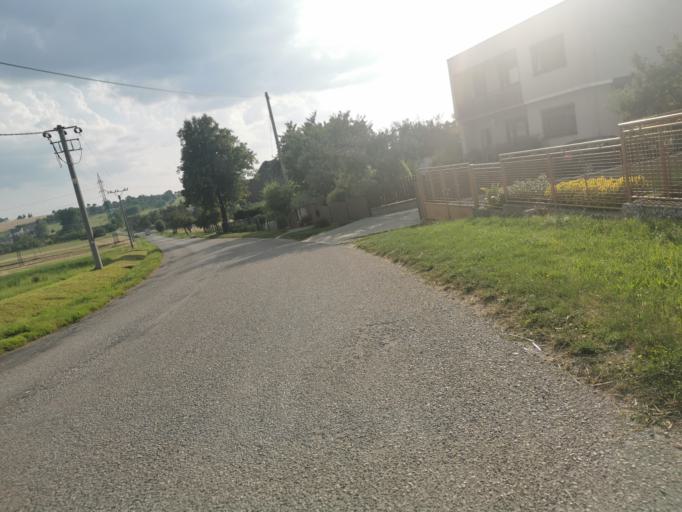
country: SK
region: Trenciansky
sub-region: Okres Myjava
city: Myjava
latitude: 48.7757
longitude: 17.6072
